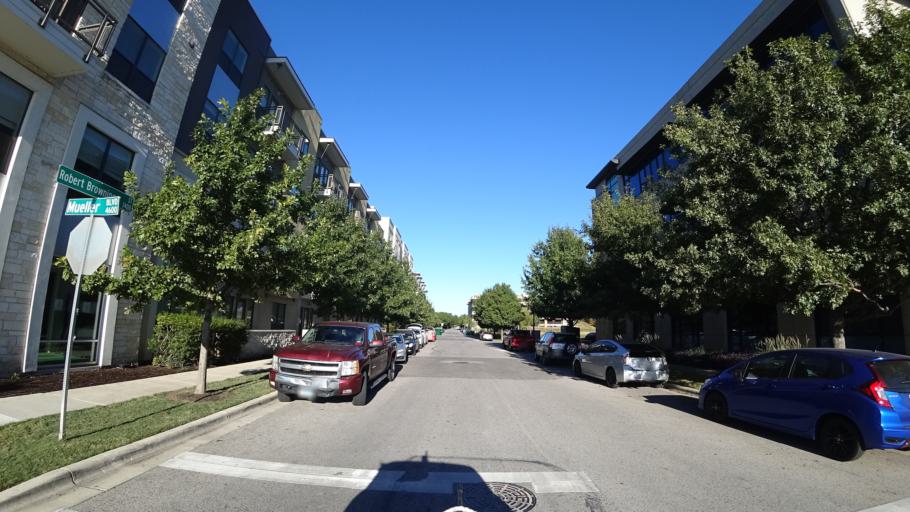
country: US
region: Texas
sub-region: Travis County
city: Austin
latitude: 30.3003
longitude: -97.7065
